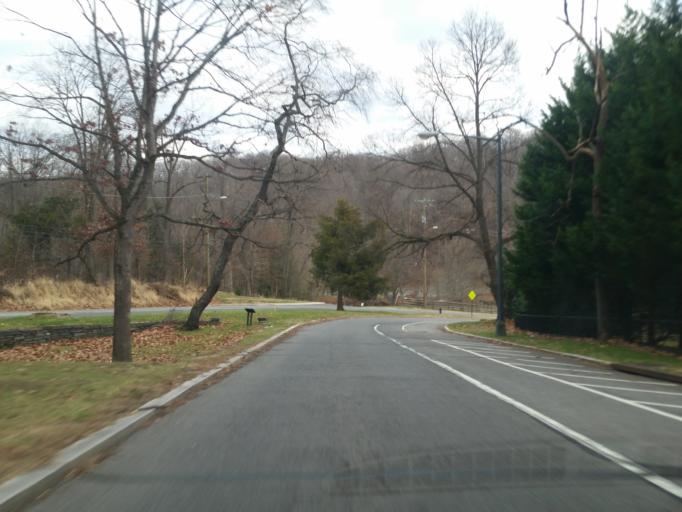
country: US
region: Maryland
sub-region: Montgomery County
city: Chevy Chase
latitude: 38.9408
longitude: -77.0537
